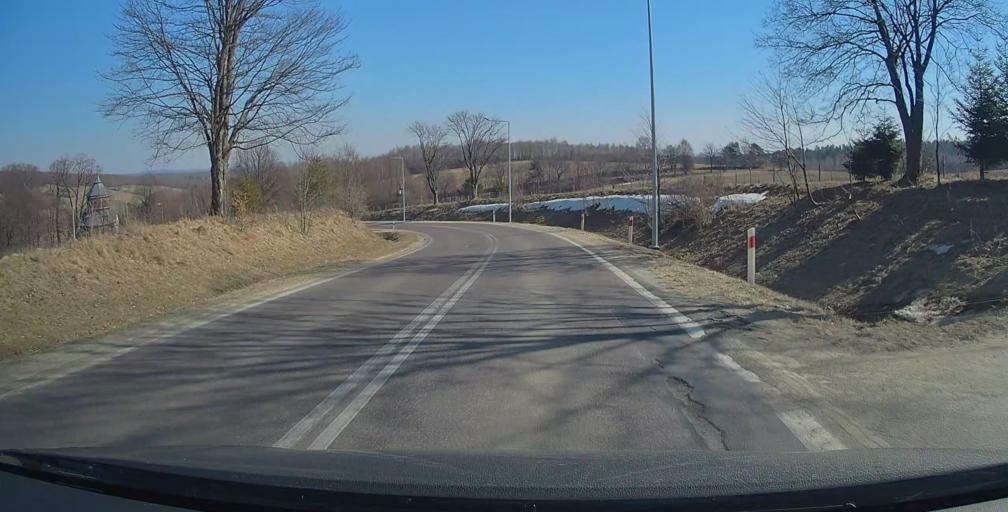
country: PL
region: Subcarpathian Voivodeship
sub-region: Powiat przemyski
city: Bircza
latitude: 49.6021
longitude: 22.4598
